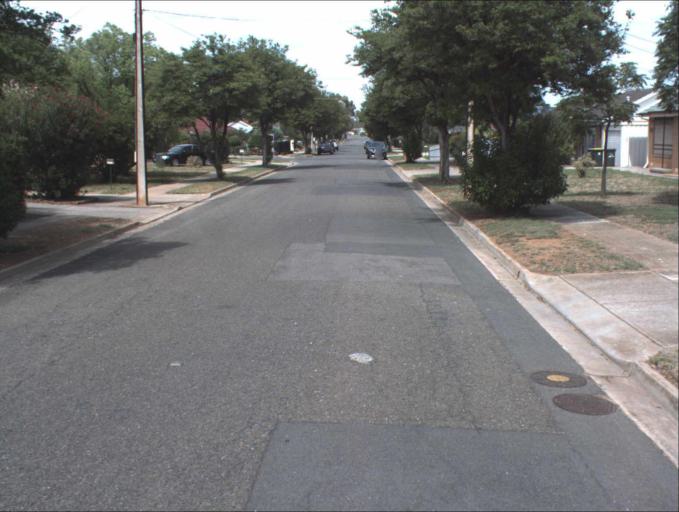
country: AU
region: South Australia
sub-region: Port Adelaide Enfield
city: Enfield
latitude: -34.8446
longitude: 138.6041
